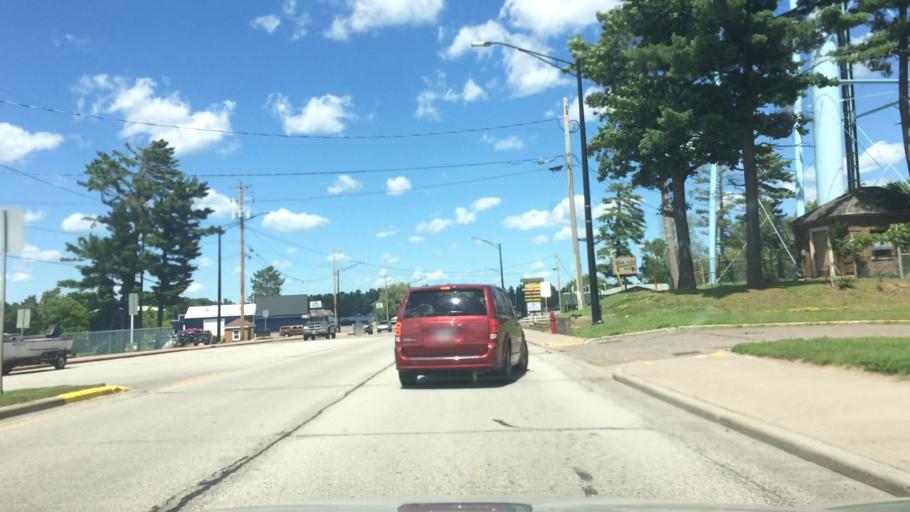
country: US
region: Wisconsin
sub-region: Vilas County
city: Lac du Flambeau
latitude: 45.8726
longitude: -89.7072
